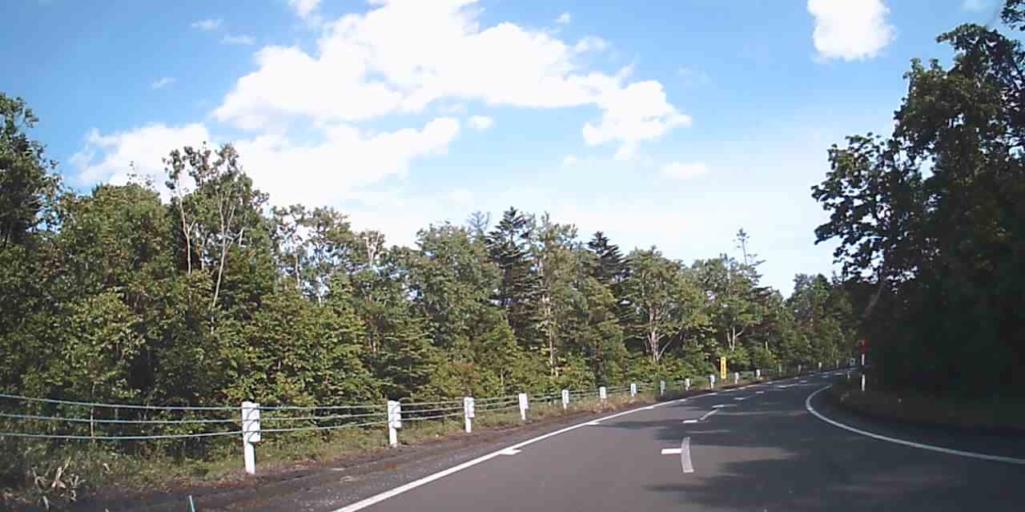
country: JP
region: Hokkaido
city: Shiraoi
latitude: 42.6831
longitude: 141.4408
